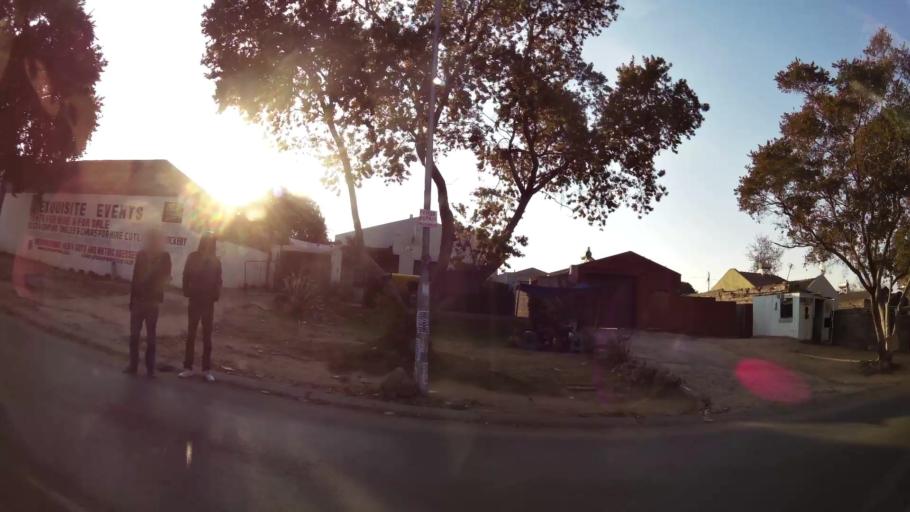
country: ZA
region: Gauteng
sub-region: Ekurhuleni Metropolitan Municipality
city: Tembisa
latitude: -26.0202
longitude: 28.1758
